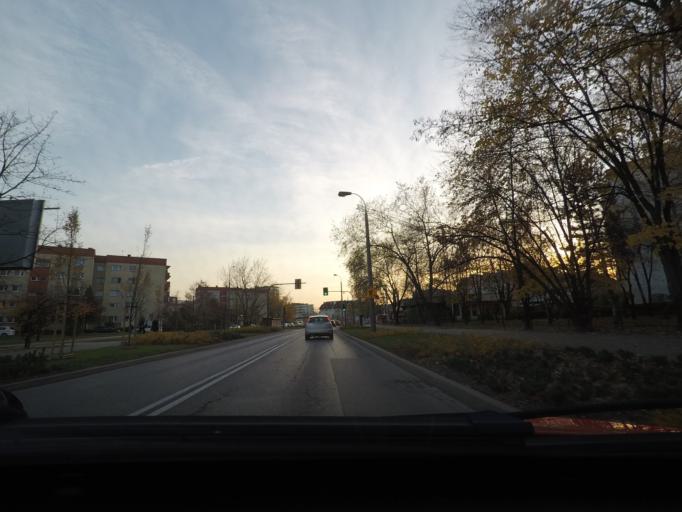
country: PL
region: Lesser Poland Voivodeship
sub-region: Krakow
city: Krakow
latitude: 50.0306
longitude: 19.9197
